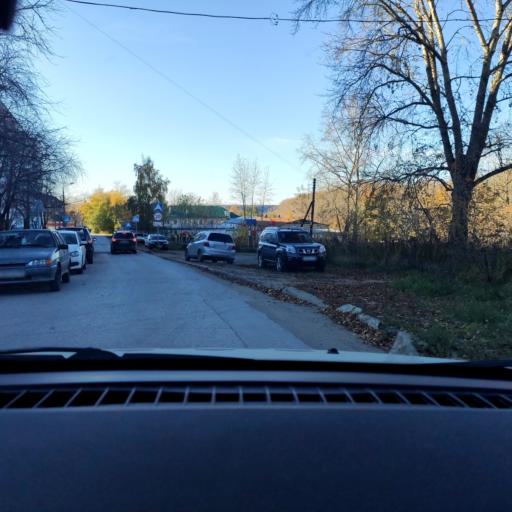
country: RU
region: Perm
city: Perm
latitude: 58.1137
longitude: 56.3773
